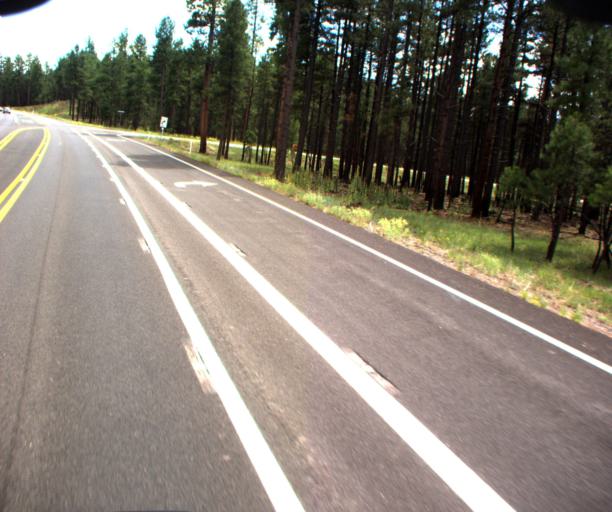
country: US
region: Arizona
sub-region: Coconino County
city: Flagstaff
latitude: 35.2614
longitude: -111.7049
